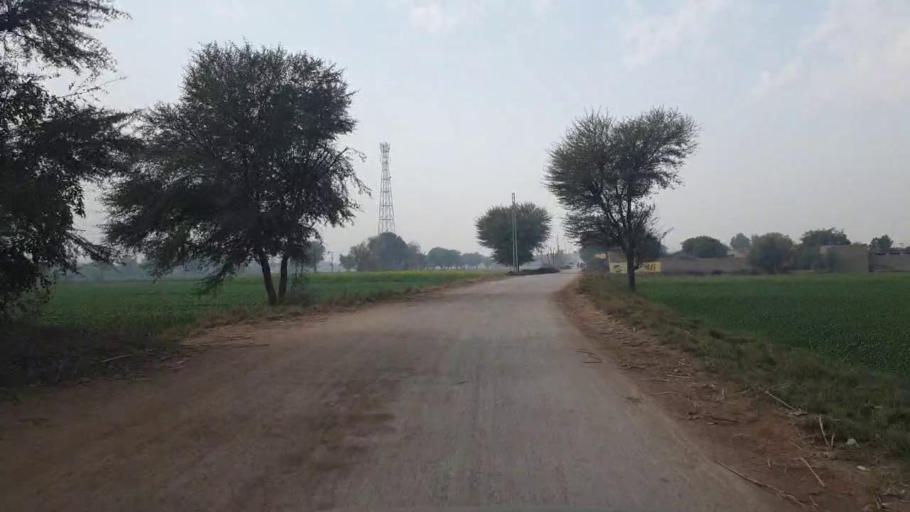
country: PK
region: Sindh
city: Hala
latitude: 25.8950
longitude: 68.4074
